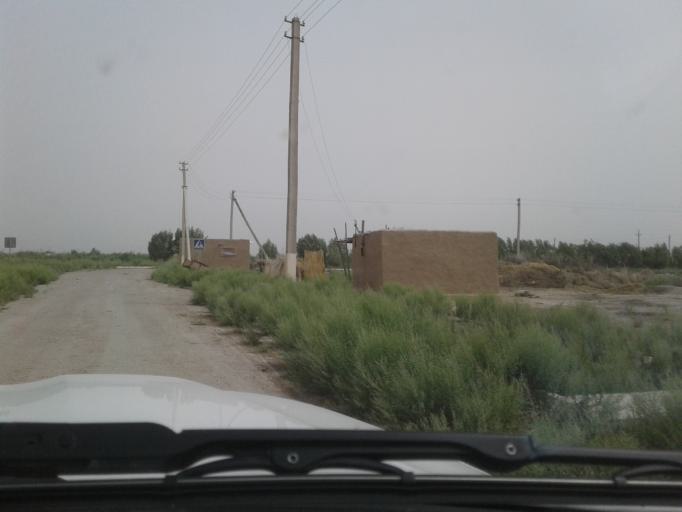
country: TM
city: Akdepe
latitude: 41.5950
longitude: 58.6126
